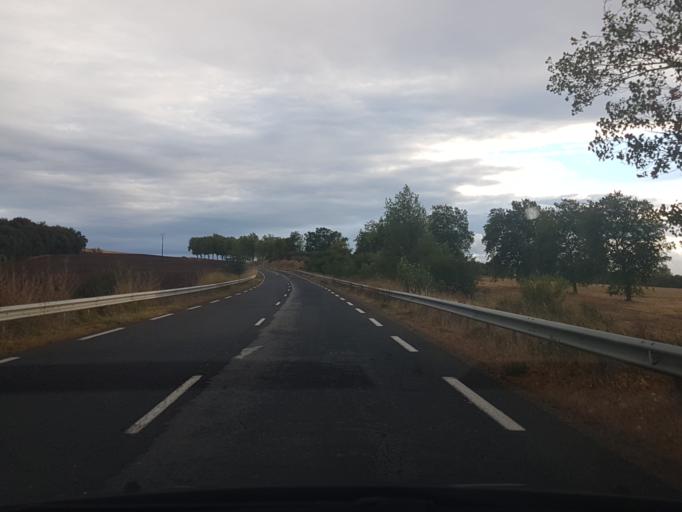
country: FR
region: Languedoc-Roussillon
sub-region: Departement de l'Aude
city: Saint-Martin-Lalande
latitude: 43.1699
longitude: 1.9997
